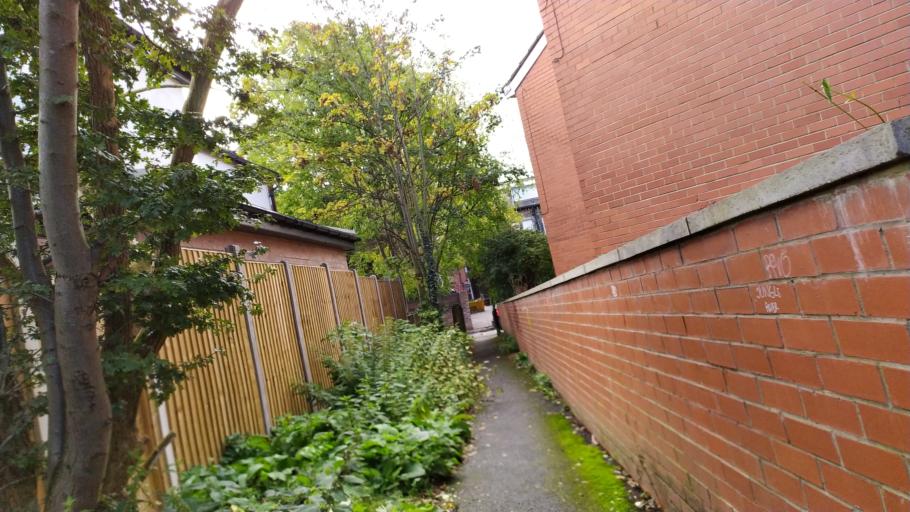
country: GB
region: England
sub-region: City and Borough of Leeds
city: Leeds
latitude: 53.8188
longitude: -1.5786
